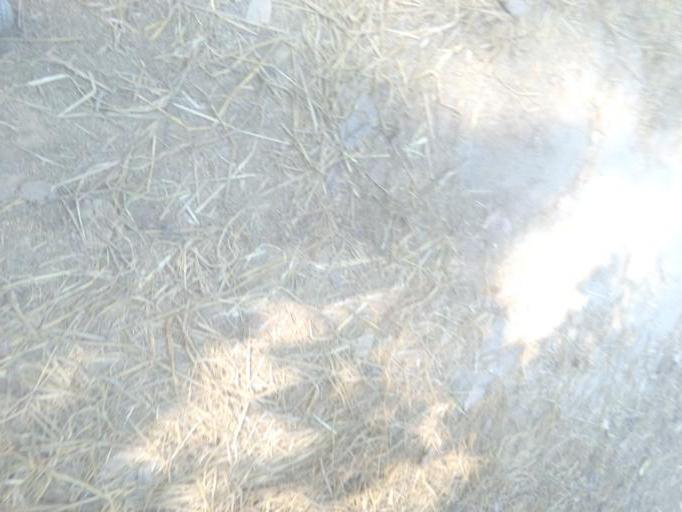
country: IN
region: Tripura
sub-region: West Tripura
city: Sonamura
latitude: 23.3215
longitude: 91.2757
